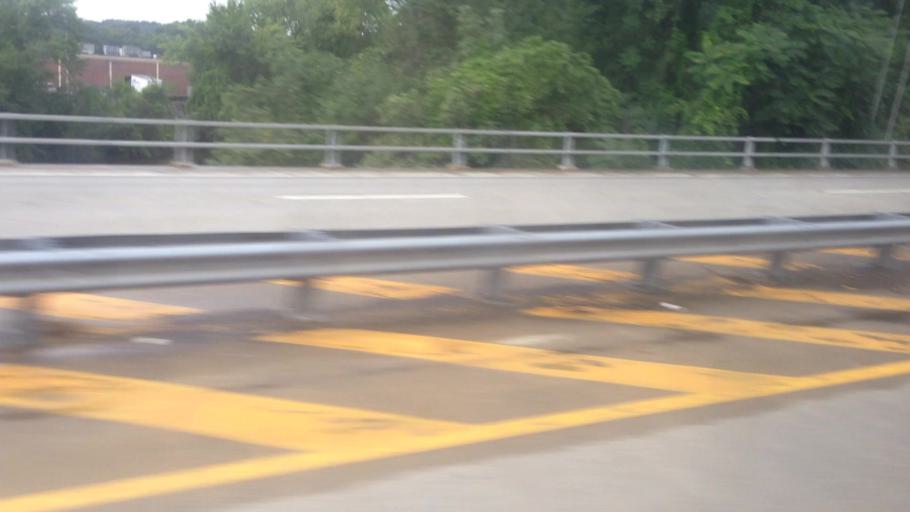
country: US
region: New York
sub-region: Ulster County
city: Kingston
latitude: 41.9392
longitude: -74.0186
